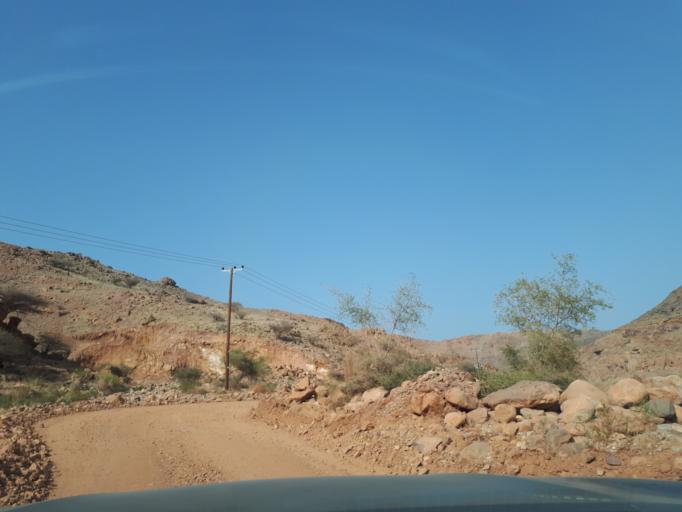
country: OM
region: Ash Sharqiyah
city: Al Qabil
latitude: 23.0707
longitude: 58.9950
